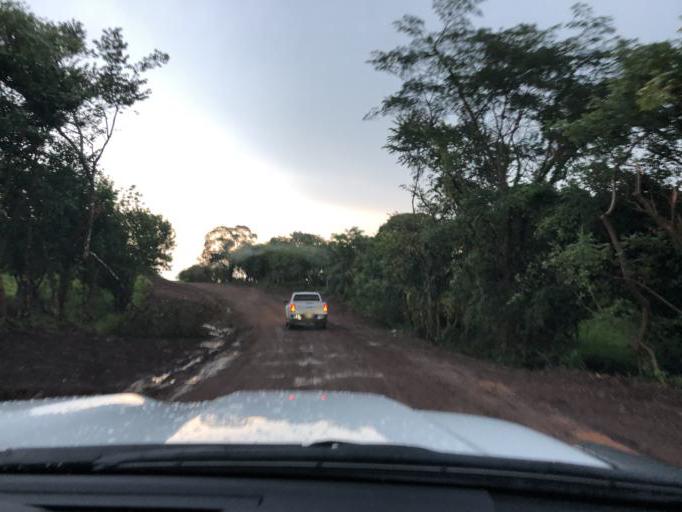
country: NI
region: Chontales
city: La Libertad
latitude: 12.1749
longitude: -85.1771
